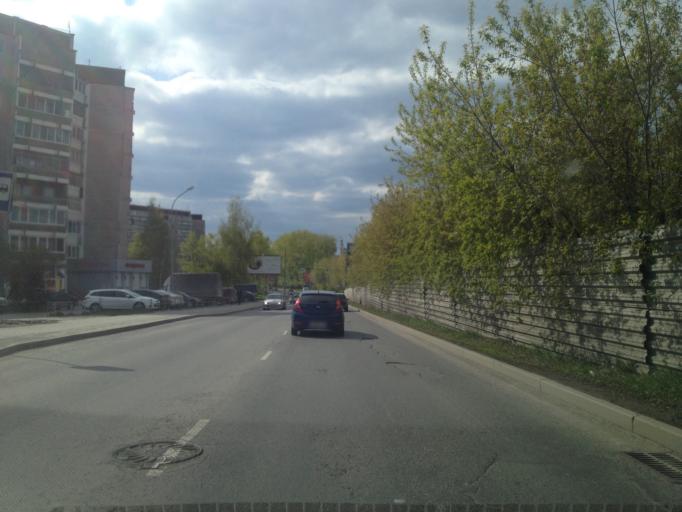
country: RU
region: Sverdlovsk
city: Yekaterinburg
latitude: 56.8564
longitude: 60.5737
